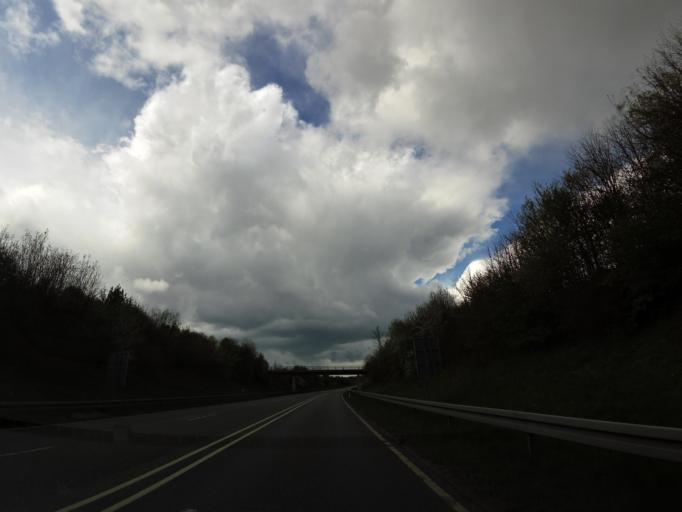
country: DE
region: Lower Saxony
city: Langelsheim
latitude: 51.9350
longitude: 10.3146
